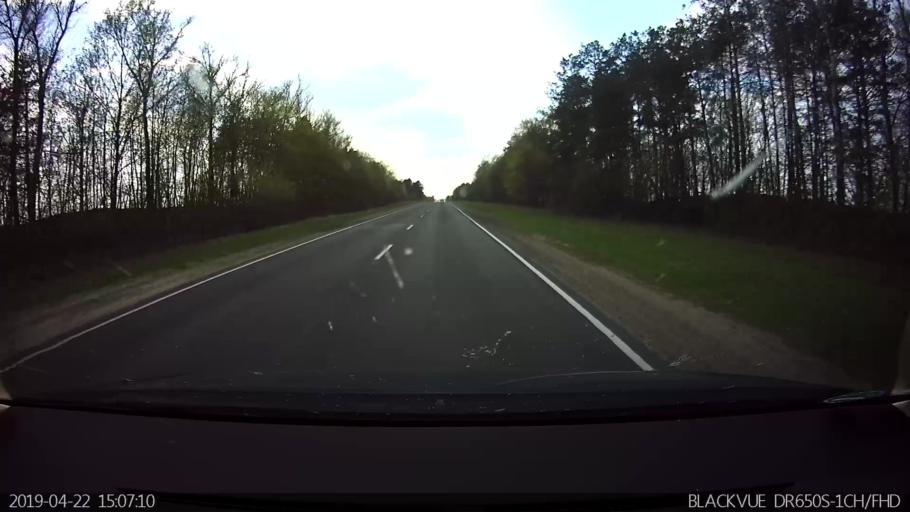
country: BY
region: Brest
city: Kamyanyets
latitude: 52.3295
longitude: 23.8159
